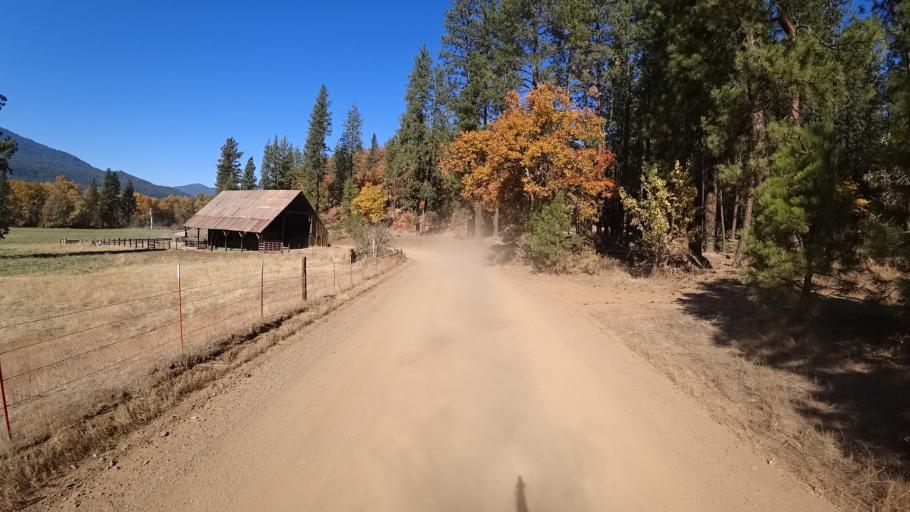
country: US
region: California
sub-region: Siskiyou County
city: Yreka
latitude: 41.6173
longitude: -122.9616
